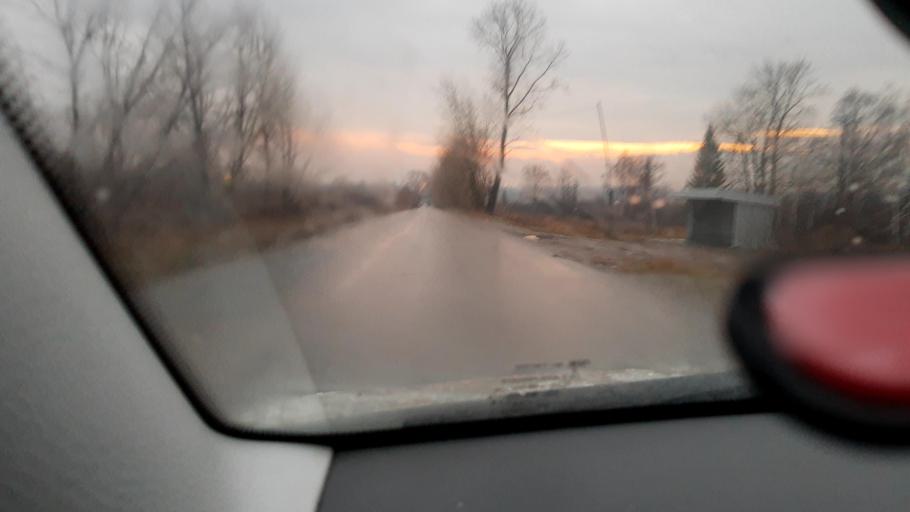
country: RU
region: Bashkortostan
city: Ufa
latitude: 54.8828
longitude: 56.1344
